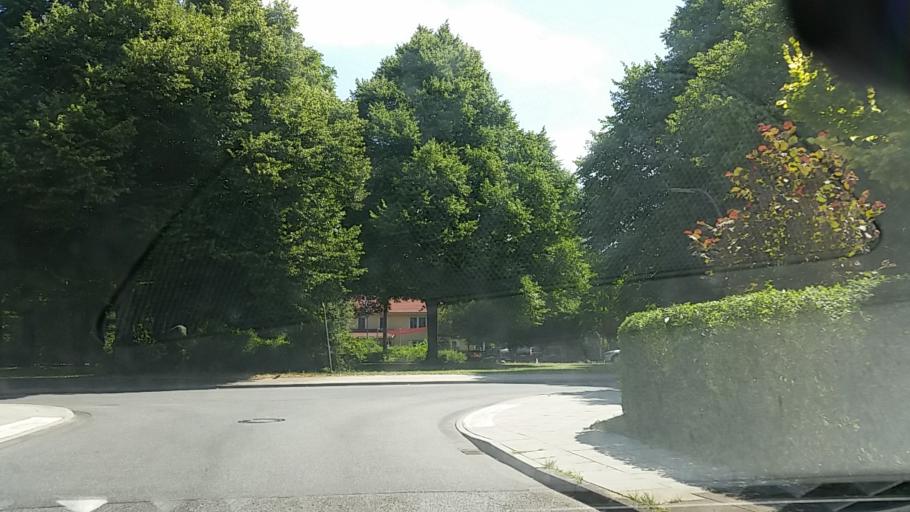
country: DE
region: Schleswig-Holstein
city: Halstenbek
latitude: 53.5805
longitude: 9.8163
